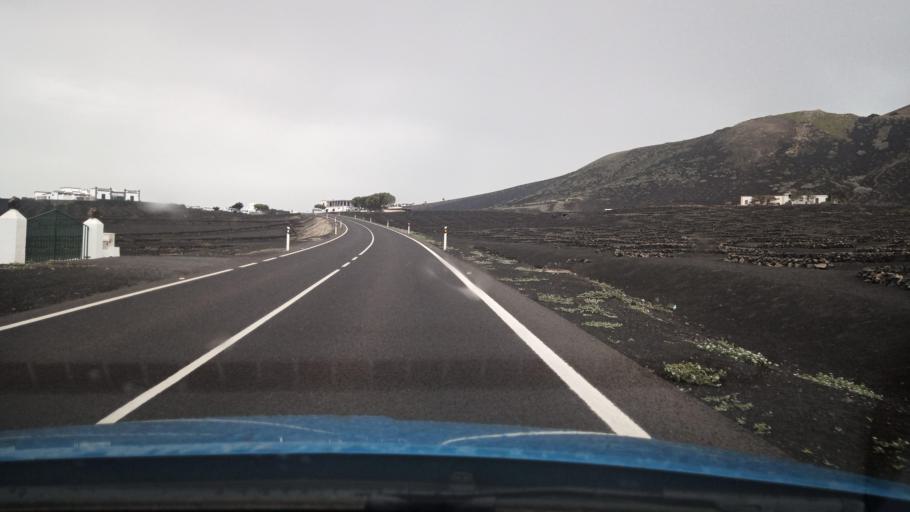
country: ES
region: Canary Islands
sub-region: Provincia de Las Palmas
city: Yaiza
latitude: 28.9673
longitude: -13.7176
